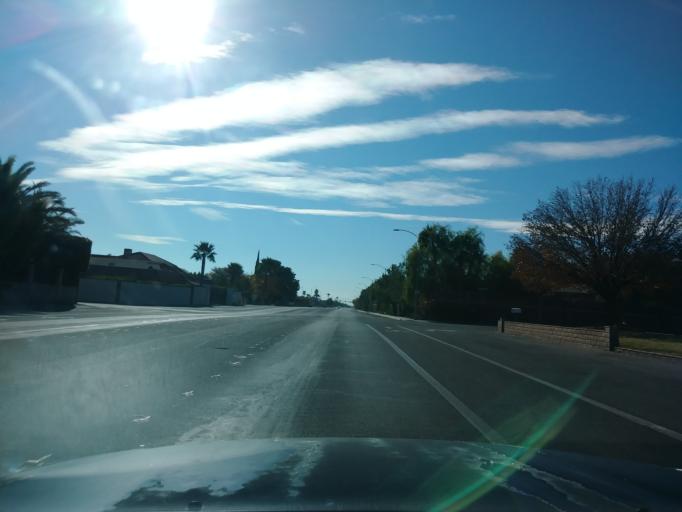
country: US
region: Nevada
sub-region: Clark County
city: Spring Valley
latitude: 36.1481
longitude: -115.2704
